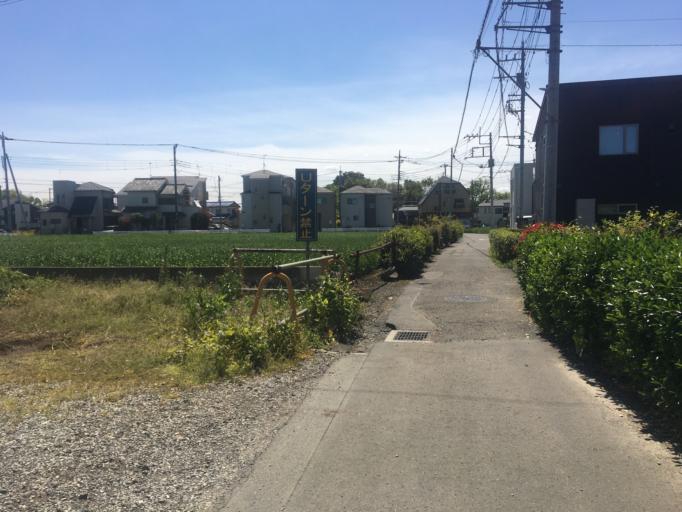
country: JP
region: Saitama
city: Shiki
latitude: 35.8390
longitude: 139.5593
